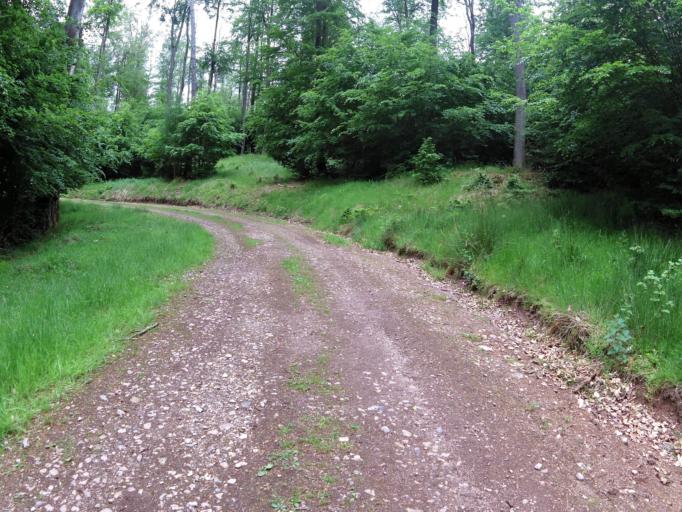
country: DE
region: Thuringia
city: Eisenach
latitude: 50.9452
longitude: 10.3167
